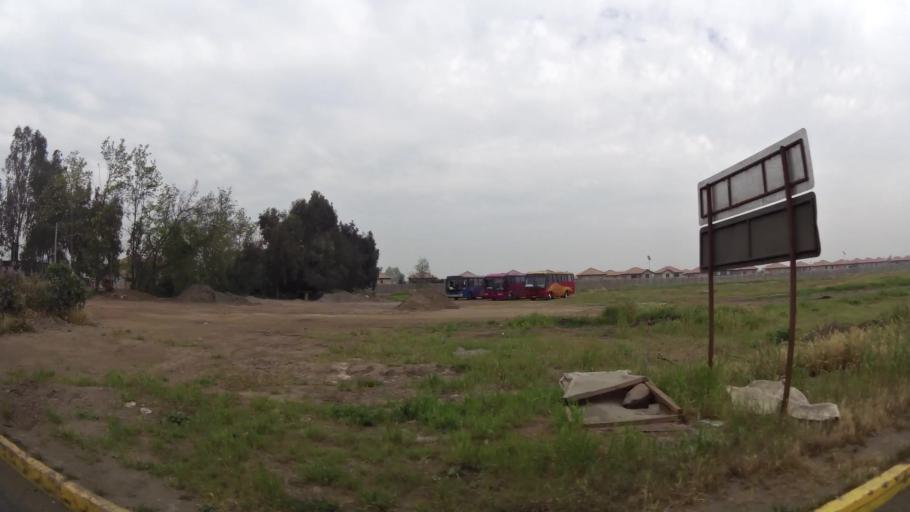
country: CL
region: Santiago Metropolitan
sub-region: Provincia de Chacabuco
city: Chicureo Abajo
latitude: -33.2164
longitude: -70.6703
